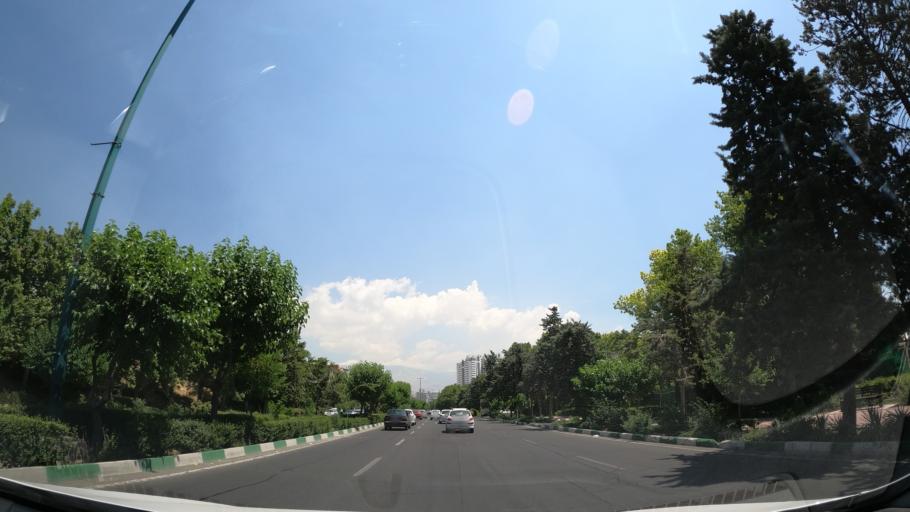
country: IR
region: Tehran
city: Tajrish
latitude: 35.7627
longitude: 51.3764
